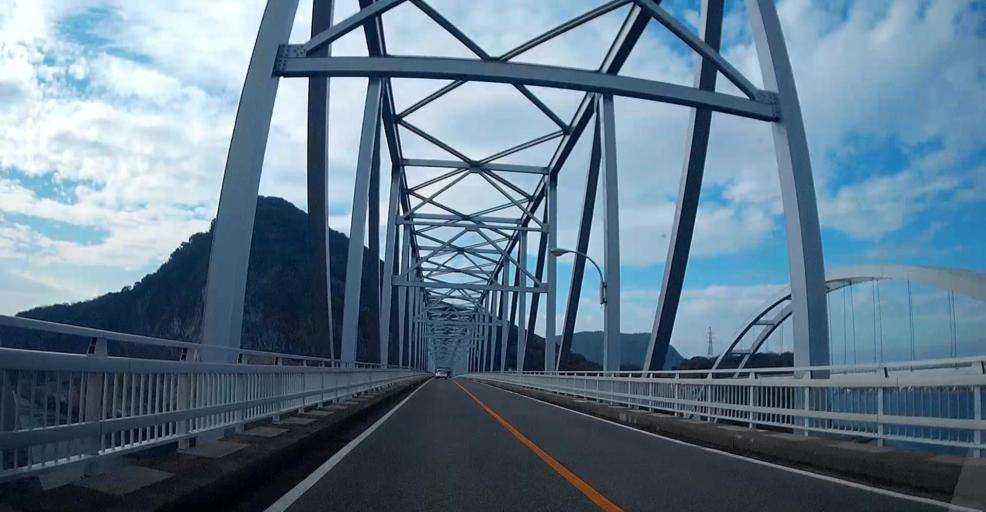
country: JP
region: Kumamoto
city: Yatsushiro
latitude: 32.6108
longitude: 130.4598
